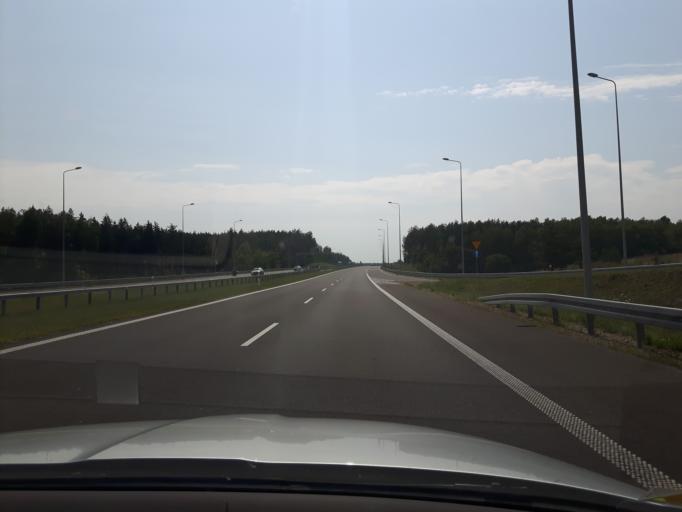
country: PL
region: Warmian-Masurian Voivodeship
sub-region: Powiat nidzicki
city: Nidzica
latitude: 53.2753
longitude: 20.4360
